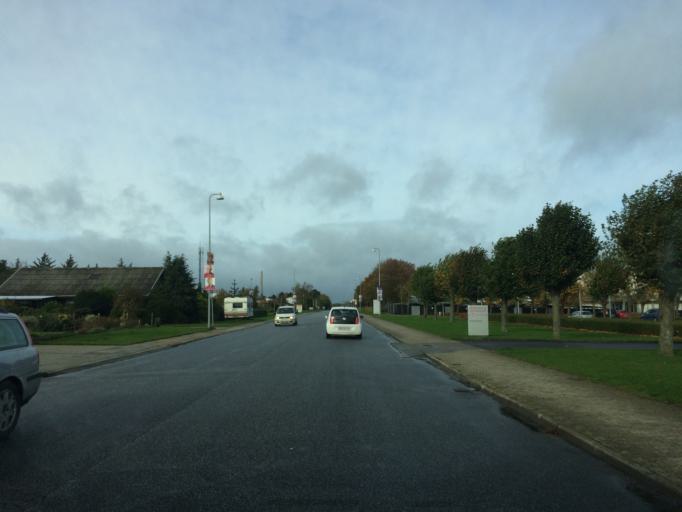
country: DK
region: South Denmark
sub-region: Fredericia Kommune
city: Fredericia
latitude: 55.5763
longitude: 9.7479
